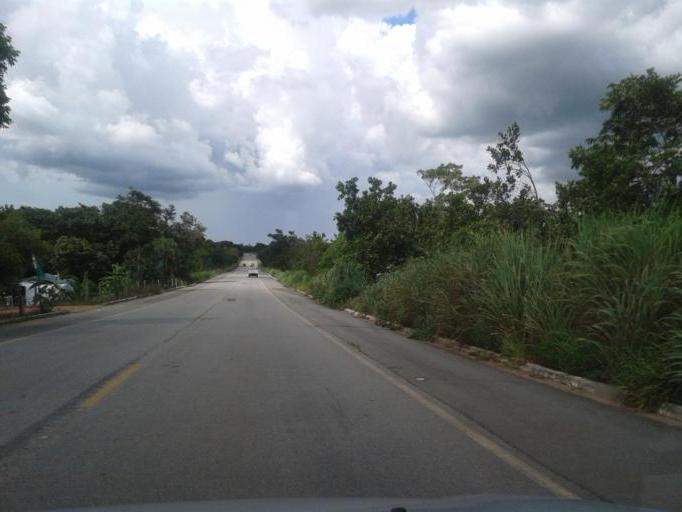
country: BR
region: Goias
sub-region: Goias
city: Goias
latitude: -15.8732
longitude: -50.0935
